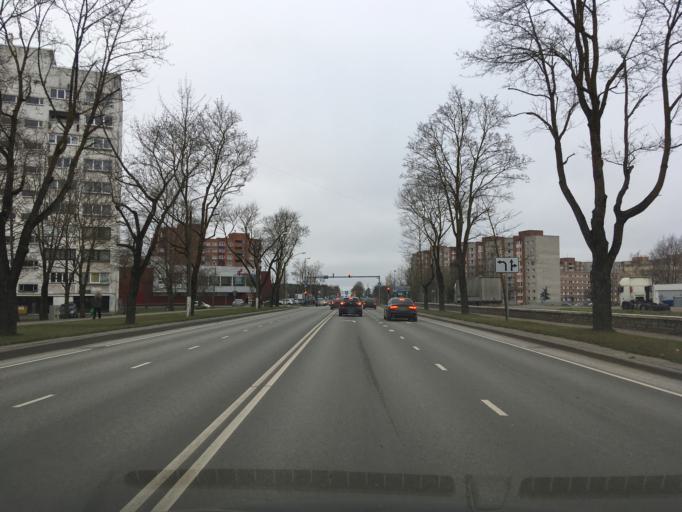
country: EE
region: Ida-Virumaa
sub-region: Narva linn
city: Narva
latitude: 59.3822
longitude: 28.1680
